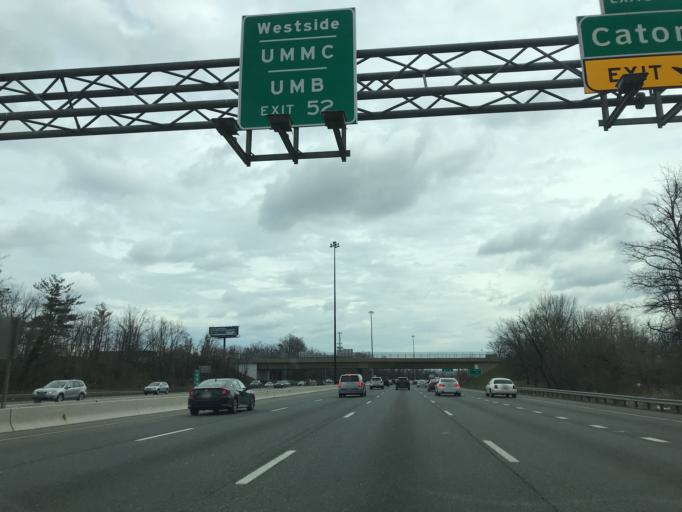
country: US
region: Maryland
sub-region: Baltimore County
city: Lansdowne
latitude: 39.2598
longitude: -76.6739
